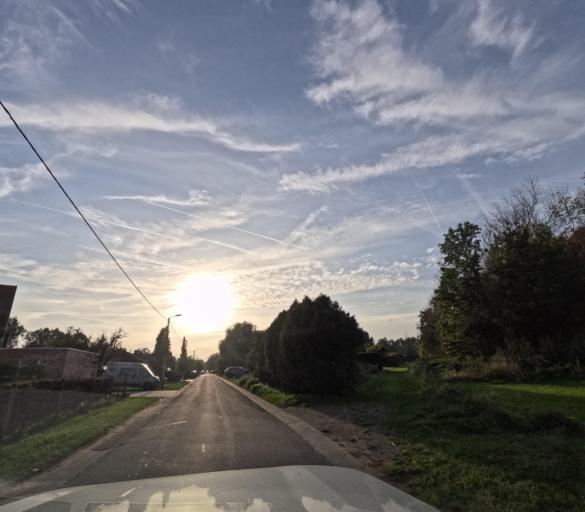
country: BE
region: Flanders
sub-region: Provincie Antwerpen
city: Heist-op-den-Berg
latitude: 51.0898
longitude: 4.7219
